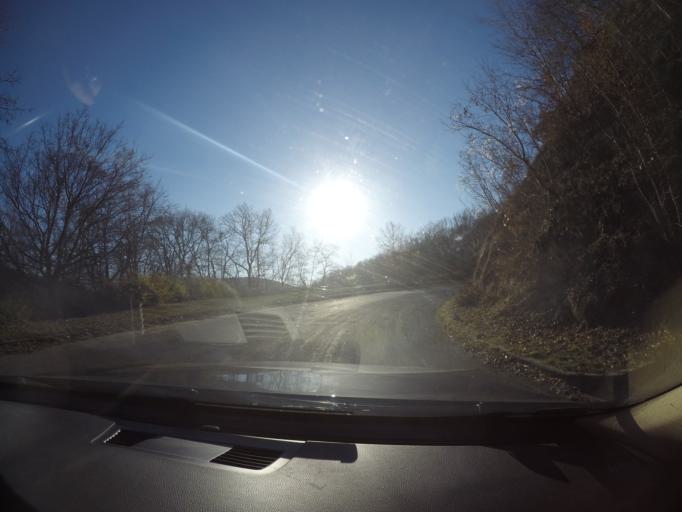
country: HU
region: Pest
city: Visegrad
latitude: 47.7930
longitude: 18.9949
